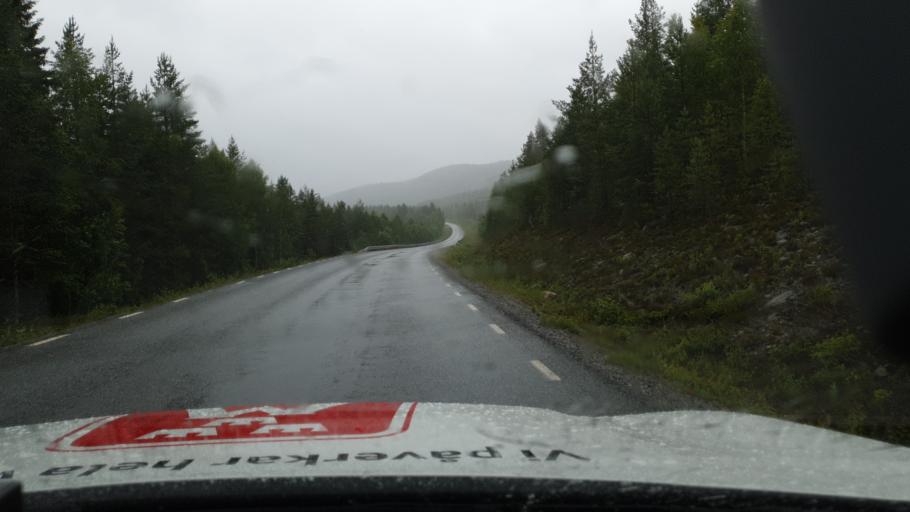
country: SE
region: Vaesterbotten
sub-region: Asele Kommun
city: Asele
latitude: 64.3173
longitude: 17.1285
